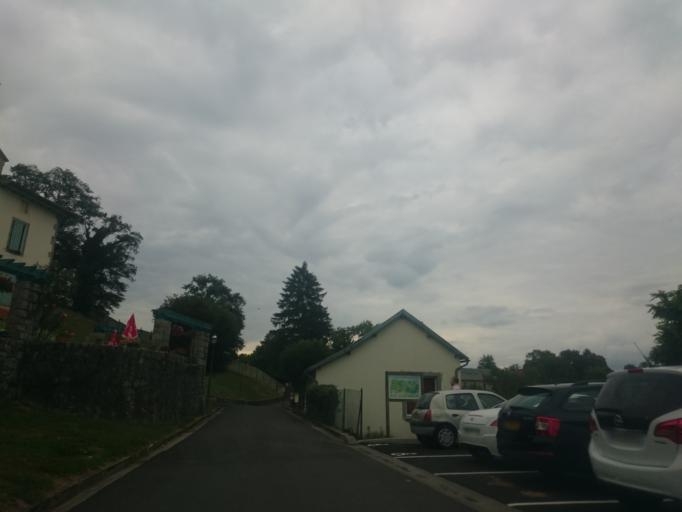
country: FR
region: Auvergne
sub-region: Departement du Cantal
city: Laroquebrou
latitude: 44.9456
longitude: 2.2237
